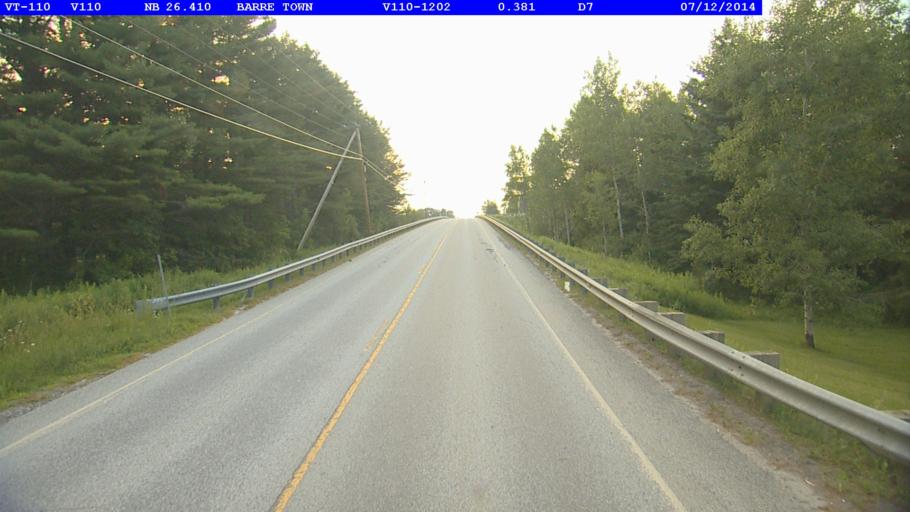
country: US
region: Vermont
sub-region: Washington County
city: South Barre
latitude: 44.1529
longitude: -72.4434
